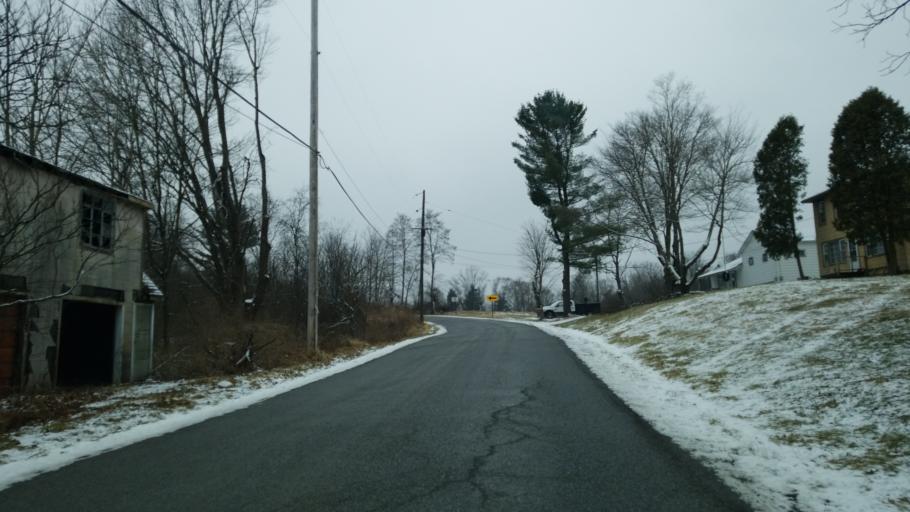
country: US
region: Pennsylvania
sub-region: Jefferson County
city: Sykesville
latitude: 41.0790
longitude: -78.7968
